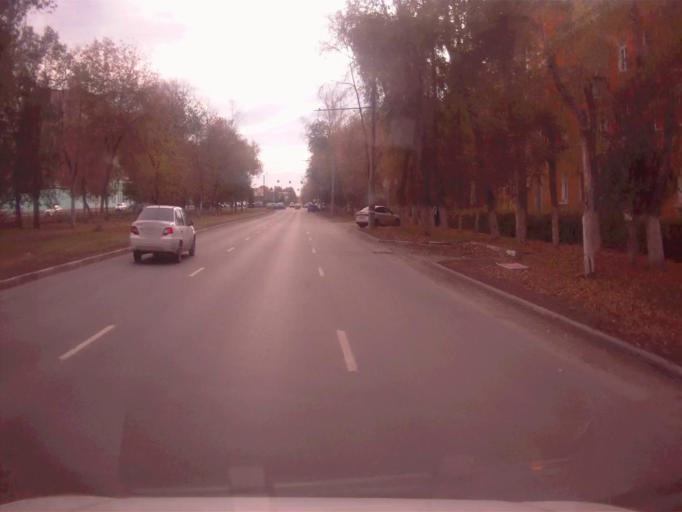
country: RU
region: Chelyabinsk
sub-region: Gorod Chelyabinsk
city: Chelyabinsk
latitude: 55.1199
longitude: 61.4718
